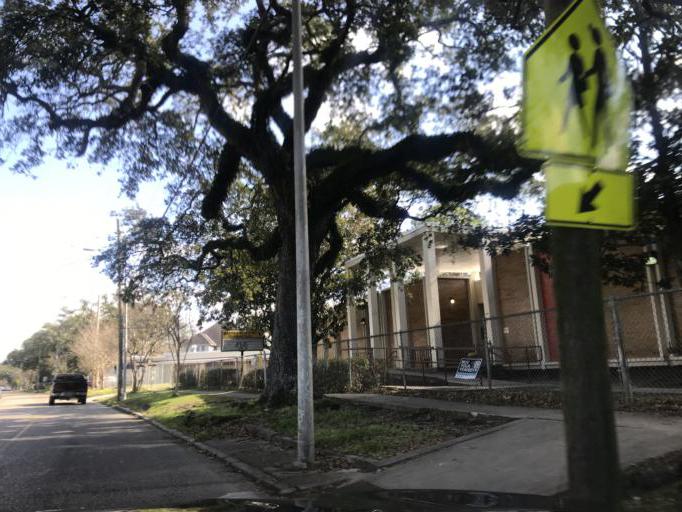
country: US
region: Louisiana
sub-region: Jefferson Parish
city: Metairie
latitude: 29.9870
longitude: -90.1399
